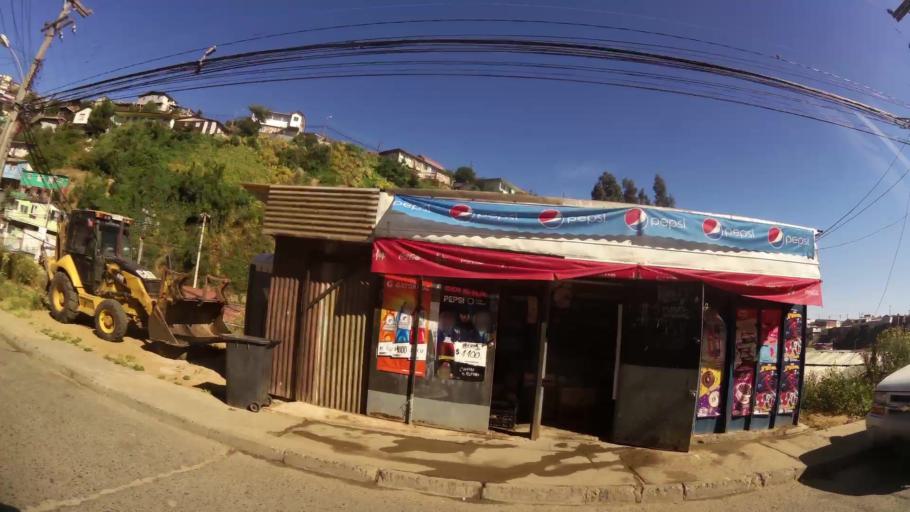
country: CL
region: Valparaiso
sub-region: Provincia de Valparaiso
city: Valparaiso
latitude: -33.0465
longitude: -71.6364
